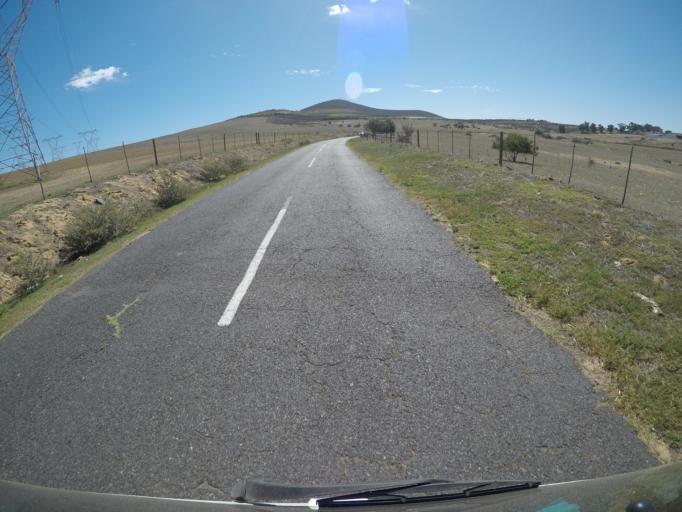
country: ZA
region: Western Cape
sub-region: City of Cape Town
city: Sunset Beach
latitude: -33.7311
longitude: 18.5653
